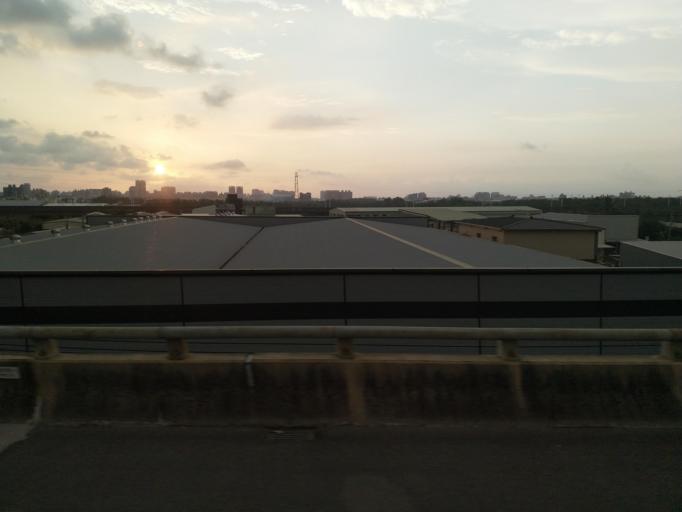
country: TW
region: Taiwan
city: Fengshan
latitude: 22.7390
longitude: 120.3616
